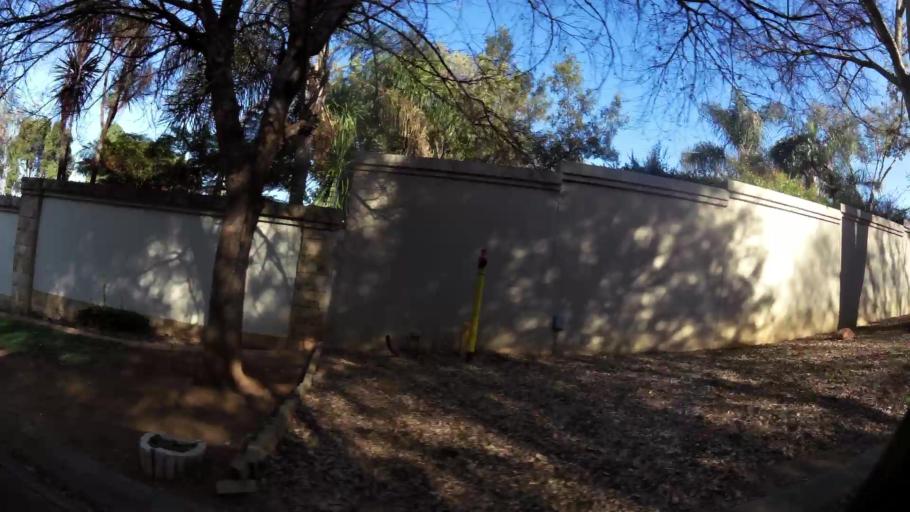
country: ZA
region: Gauteng
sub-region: City of Johannesburg Metropolitan Municipality
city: Roodepoort
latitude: -26.0897
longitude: 27.9565
